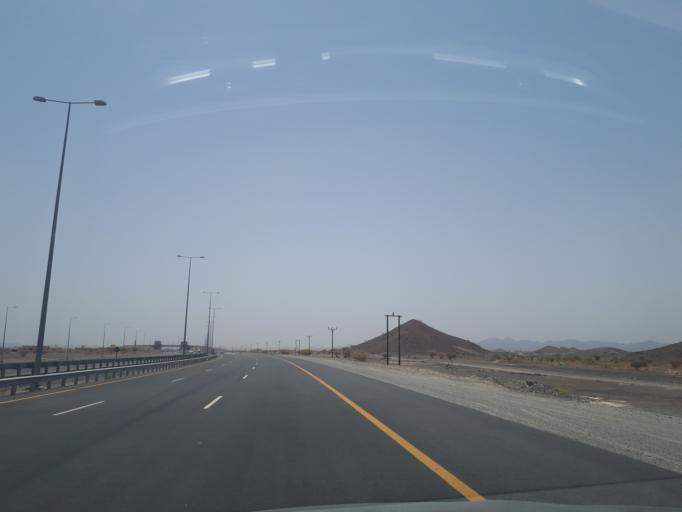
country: OM
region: Ash Sharqiyah
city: Ibra'
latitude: 22.8046
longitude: 58.4440
